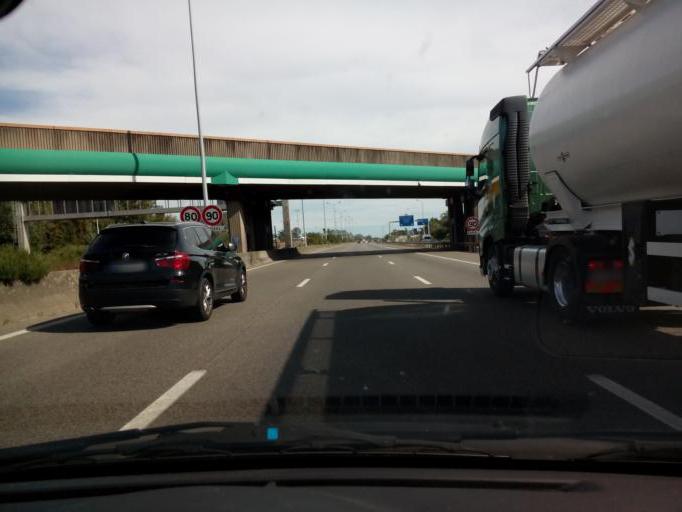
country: FR
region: Rhone-Alpes
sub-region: Departement du Rhone
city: Saint-Priest
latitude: 45.7013
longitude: 4.9699
